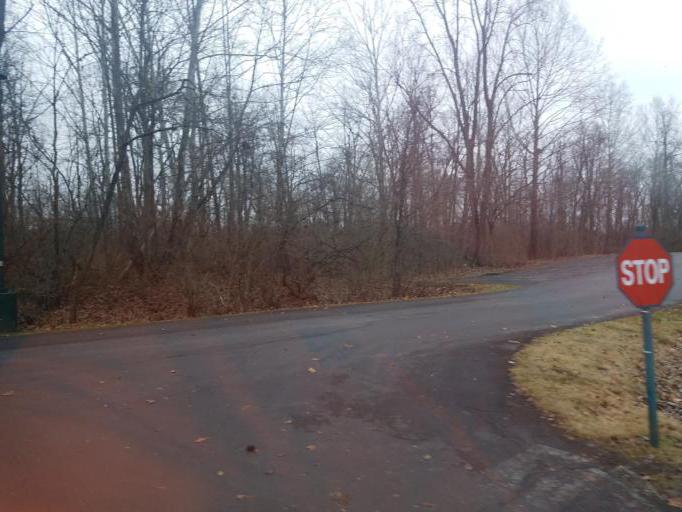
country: US
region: Ohio
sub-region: Franklin County
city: Westerville
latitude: 40.1304
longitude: -82.9450
